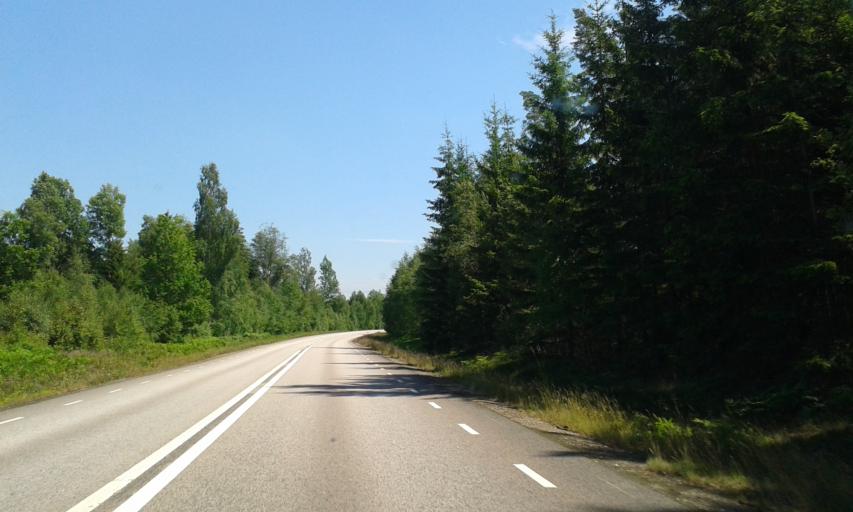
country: SE
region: Kronoberg
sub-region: Lessebo Kommun
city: Hovmantorp
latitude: 56.6847
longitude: 15.0537
